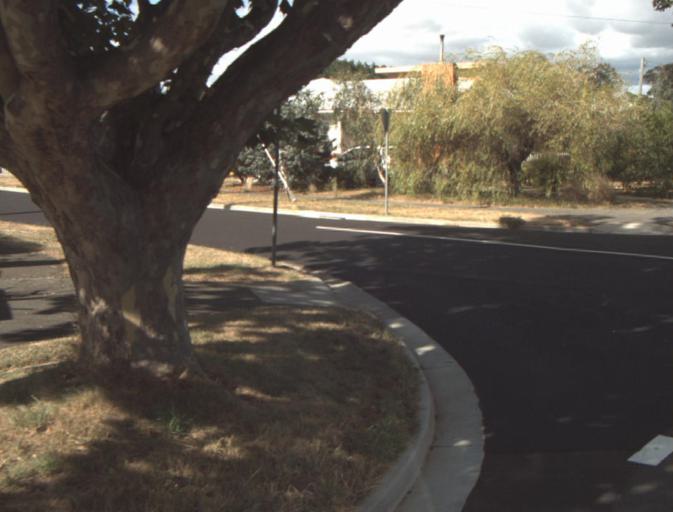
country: AU
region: Tasmania
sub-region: Launceston
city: Newstead
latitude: -41.4551
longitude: 147.1744
